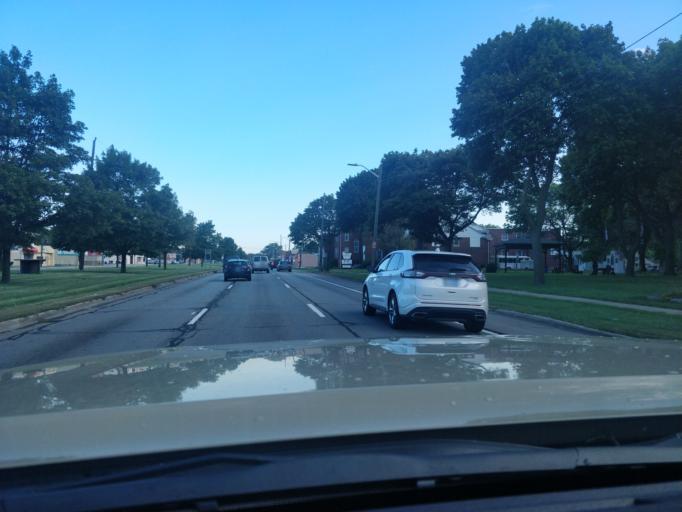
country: US
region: Michigan
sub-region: Wayne County
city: Lincoln Park
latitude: 42.2381
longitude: -83.1799
